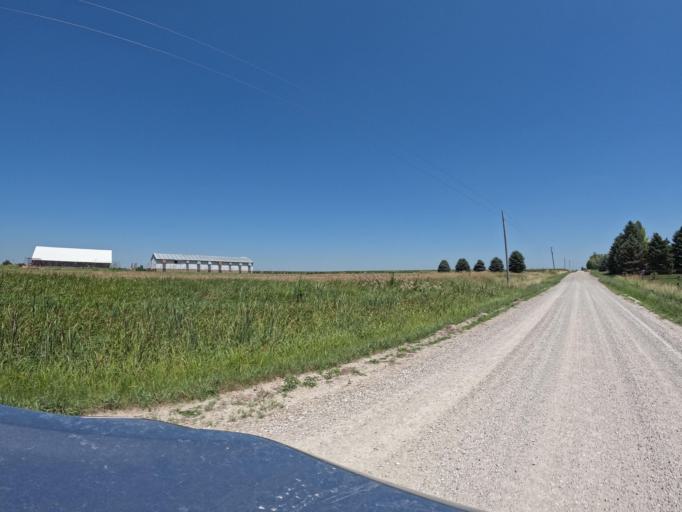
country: US
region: Iowa
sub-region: Keokuk County
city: Sigourney
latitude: 41.4234
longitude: -92.3474
